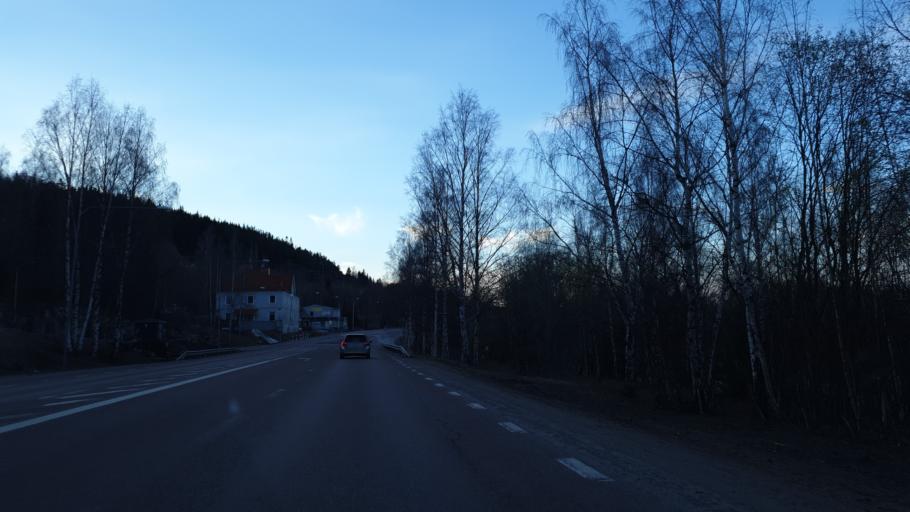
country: SE
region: Vaesternorrland
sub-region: Sundsvalls Kommun
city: Kvissleby
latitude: 62.3124
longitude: 17.3715
